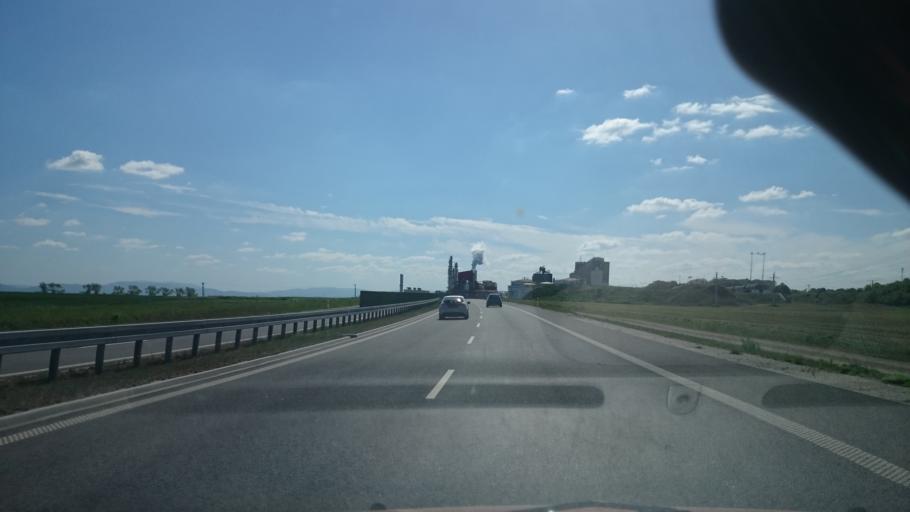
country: PL
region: Opole Voivodeship
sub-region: Powiat nyski
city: Nysa
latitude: 50.4850
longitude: 17.2701
